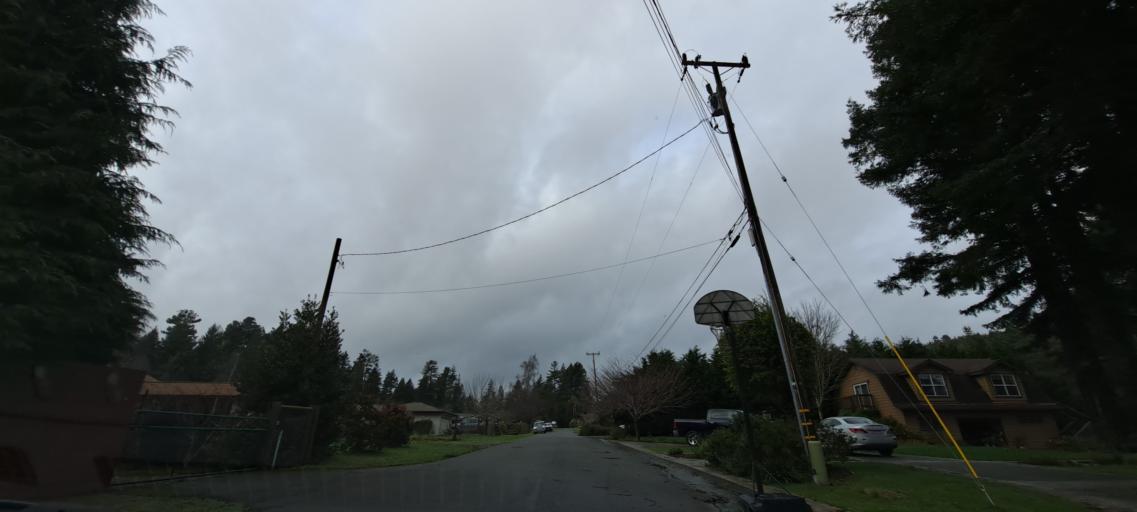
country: US
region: California
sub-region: Humboldt County
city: Fortuna
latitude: 40.6034
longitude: -124.1364
